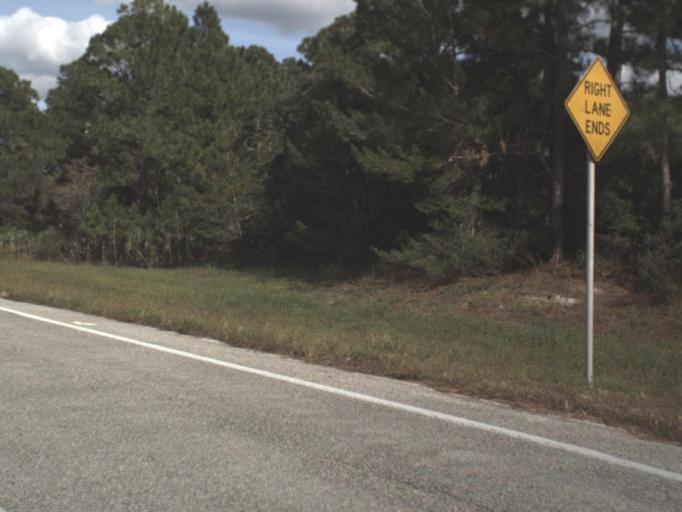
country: US
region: Florida
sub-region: Brevard County
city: Port Saint John
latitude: 28.5168
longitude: -80.8283
